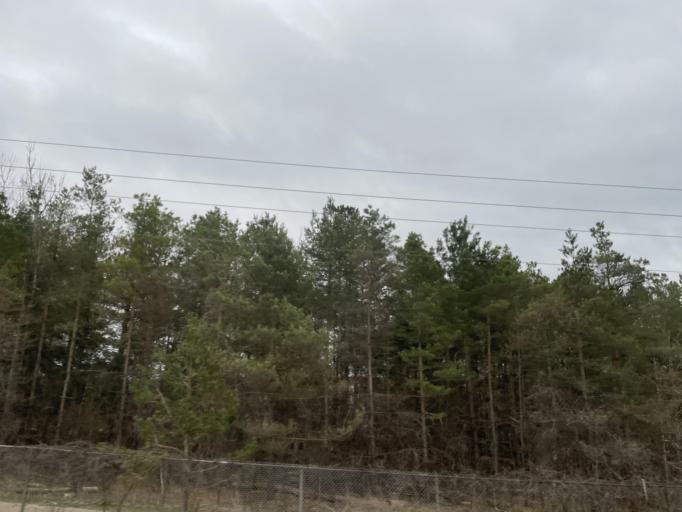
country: CA
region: Ontario
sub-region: Wellington County
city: Guelph
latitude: 43.5810
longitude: -80.2381
